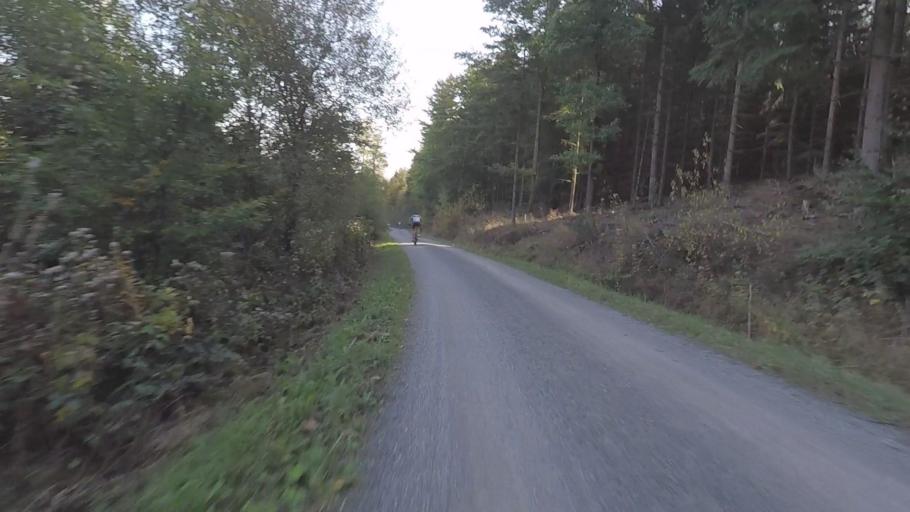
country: DE
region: Baden-Wuerttemberg
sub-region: Regierungsbezirk Stuttgart
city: Wustenrot
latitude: 49.0683
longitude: 9.4773
